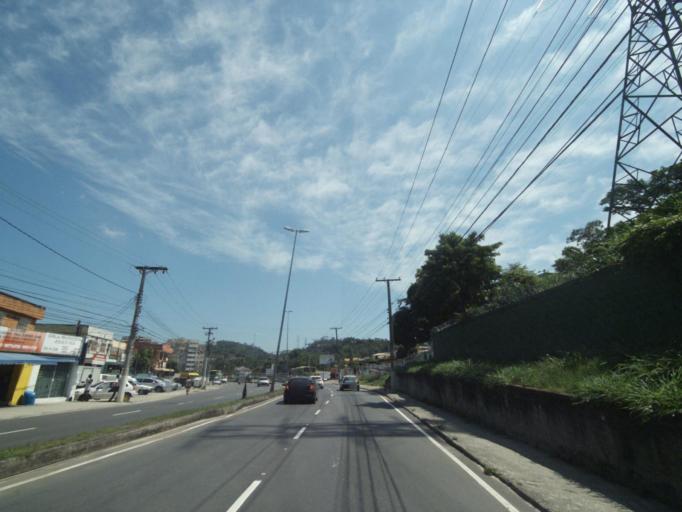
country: BR
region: Rio de Janeiro
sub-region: Sao Goncalo
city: Sao Goncalo
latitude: -22.8819
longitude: -43.0296
